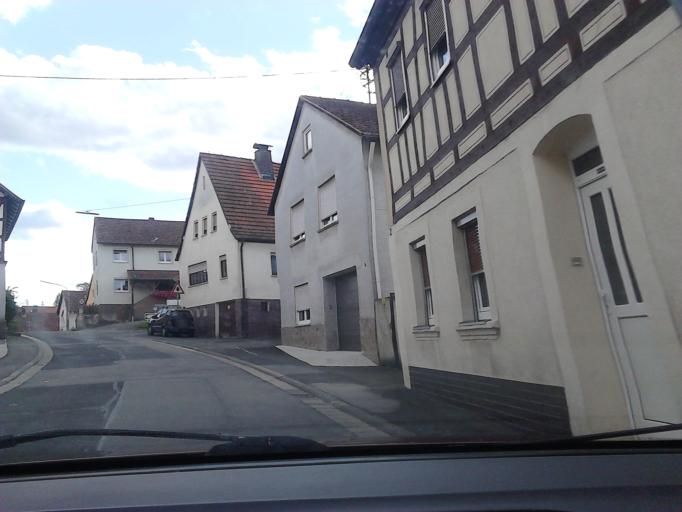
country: DE
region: Bavaria
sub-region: Regierungsbezirk Unterfranken
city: Maroldsweisach
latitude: 50.1957
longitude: 10.6592
